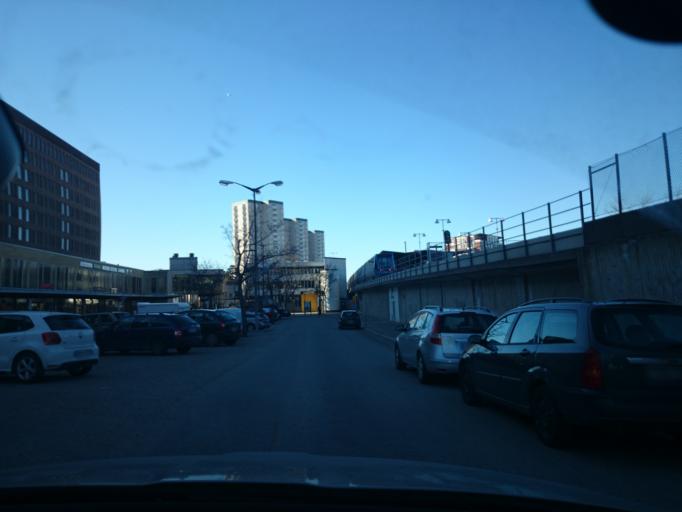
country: SE
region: Stockholm
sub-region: Stockholms Kommun
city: Arsta
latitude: 59.2423
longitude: 18.0946
